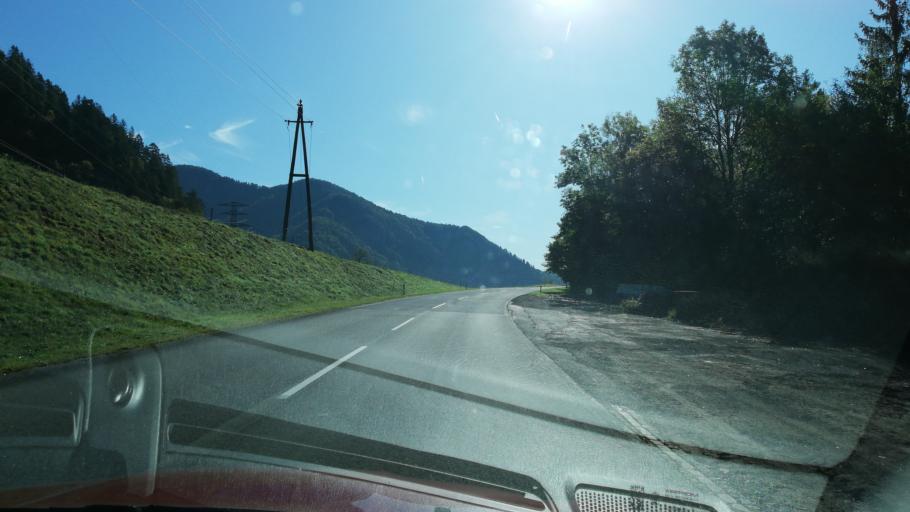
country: AT
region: Styria
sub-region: Politischer Bezirk Liezen
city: Landl
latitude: 47.6937
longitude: 14.6935
